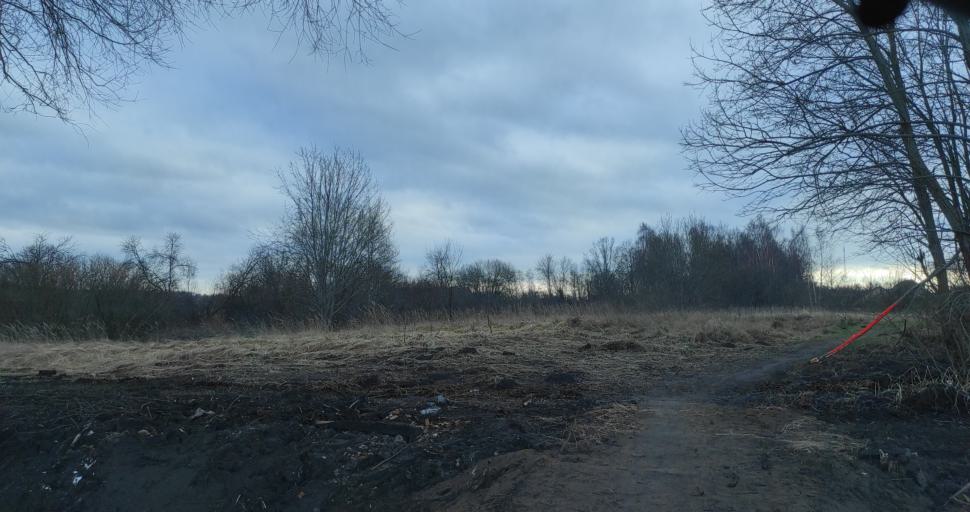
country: LV
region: Kuldigas Rajons
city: Kuldiga
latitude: 56.9563
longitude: 21.9989
